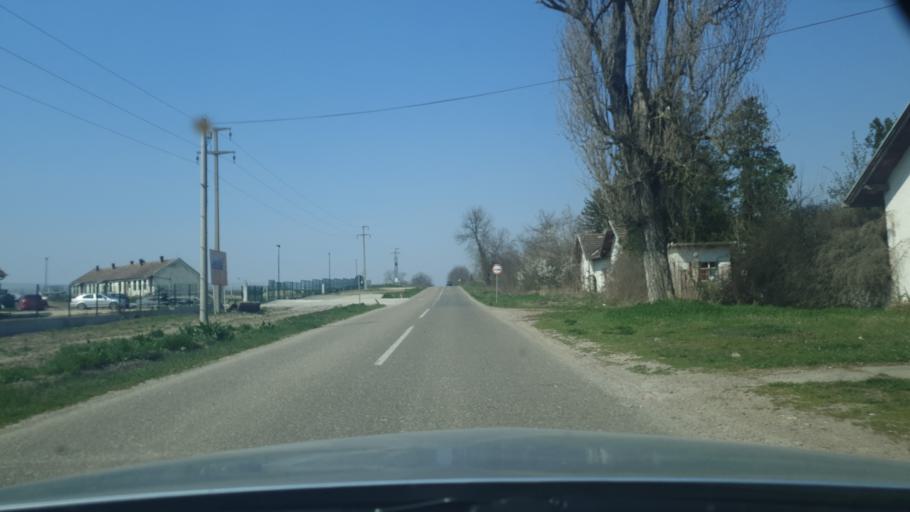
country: RS
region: Autonomna Pokrajina Vojvodina
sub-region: Sremski Okrug
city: Ruma
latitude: 45.0101
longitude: 19.7855
